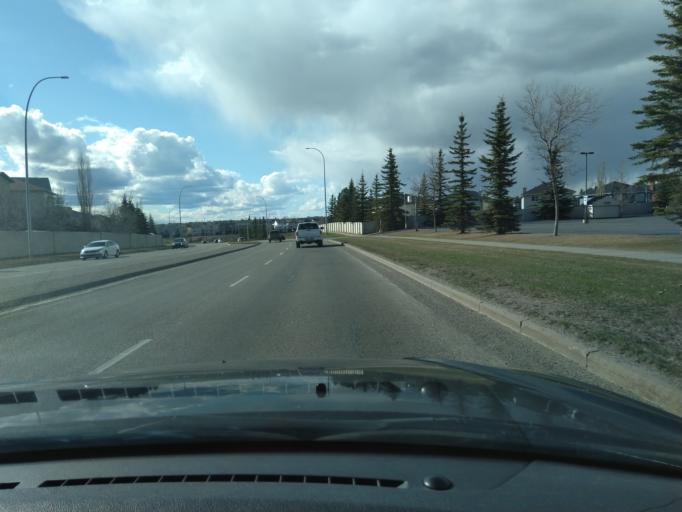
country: CA
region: Alberta
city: Calgary
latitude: 51.1424
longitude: -114.1843
